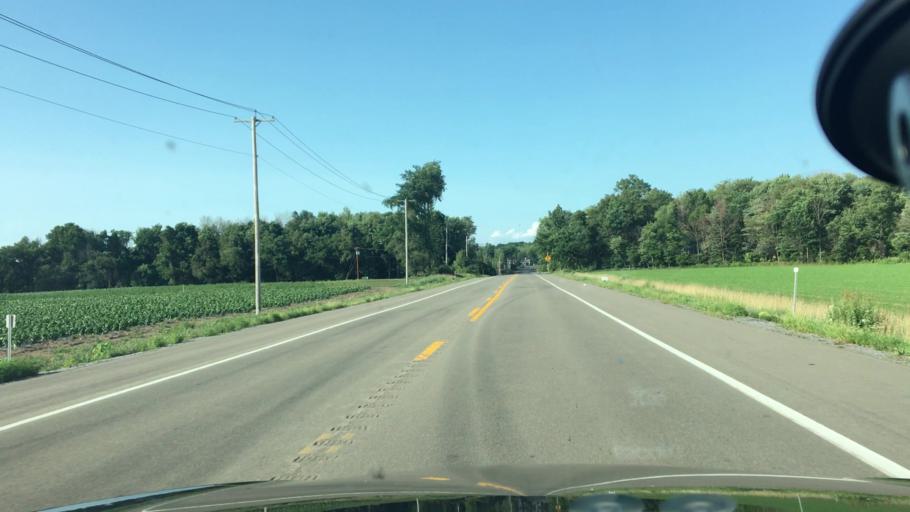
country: US
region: New York
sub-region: Erie County
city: Eden
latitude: 42.6908
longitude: -78.9395
